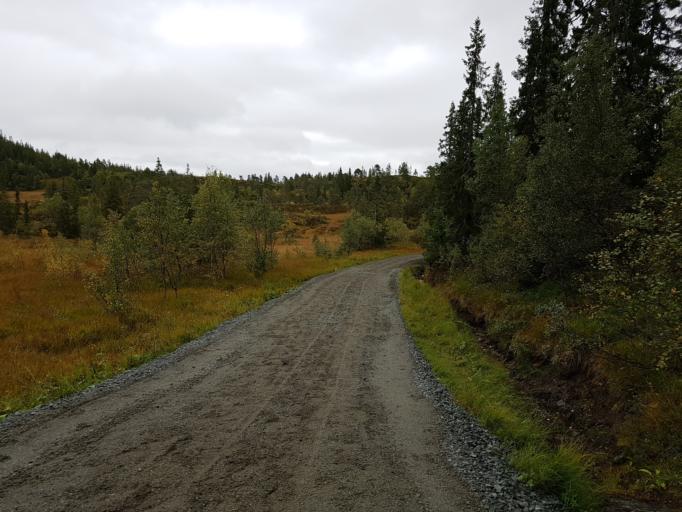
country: NO
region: Sor-Trondelag
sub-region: Melhus
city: Melhus
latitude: 63.4168
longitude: 10.2283
